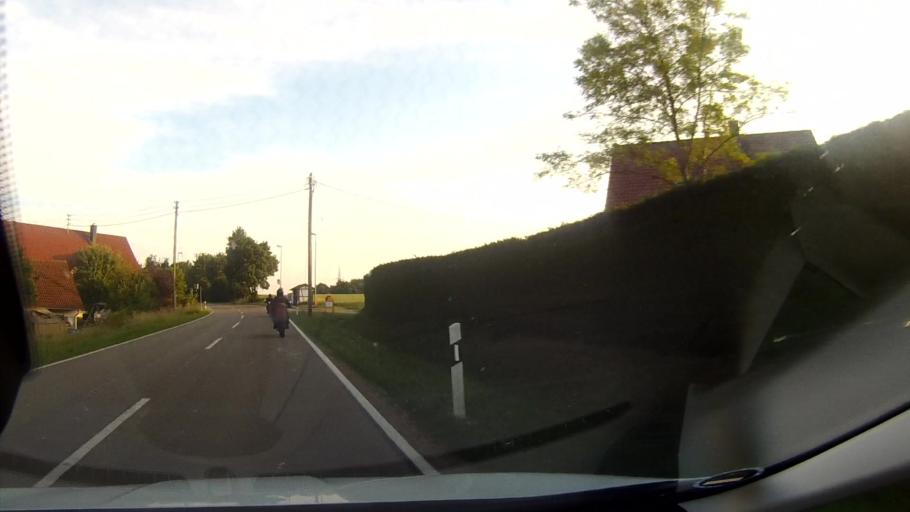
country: DE
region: Baden-Wuerttemberg
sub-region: Tuebingen Region
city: Staig
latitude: 48.3081
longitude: 10.0155
